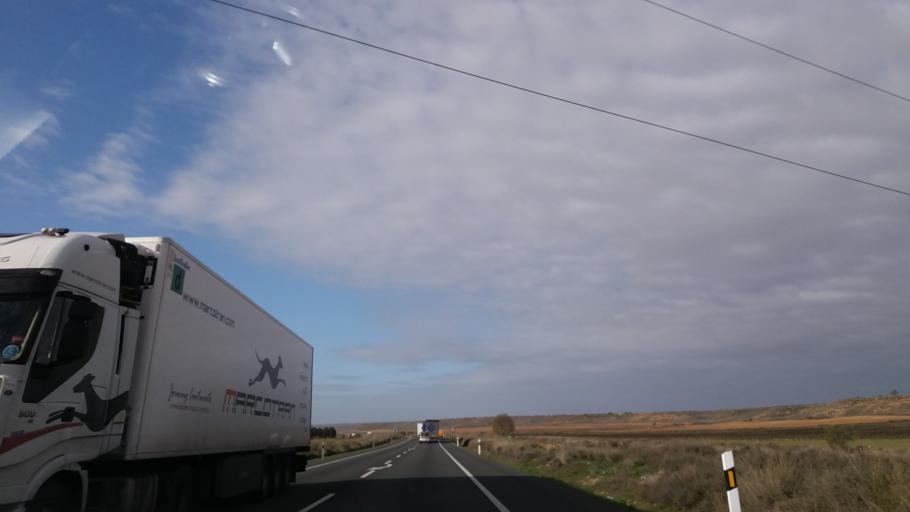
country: ES
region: Aragon
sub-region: Provincia de Huesca
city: Ballobar
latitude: 41.5205
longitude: 0.1992
